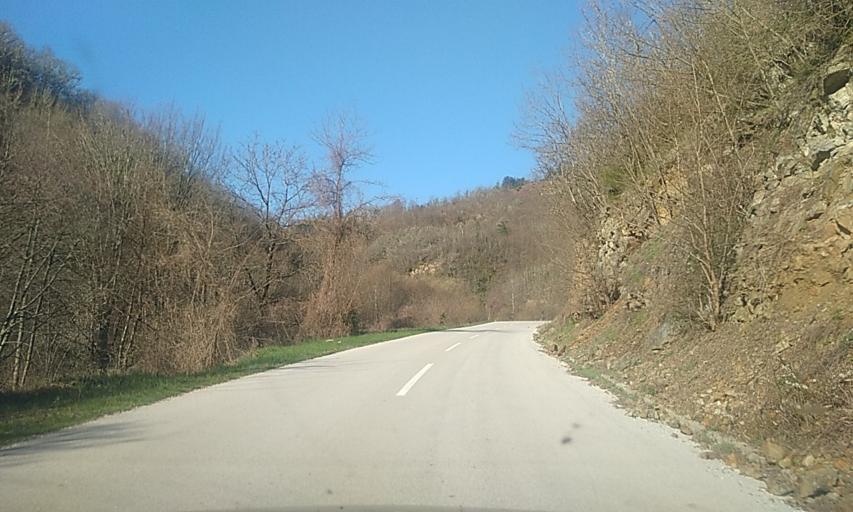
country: RS
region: Central Serbia
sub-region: Pcinjski Okrug
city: Bosilegrad
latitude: 42.4114
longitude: 22.4800
